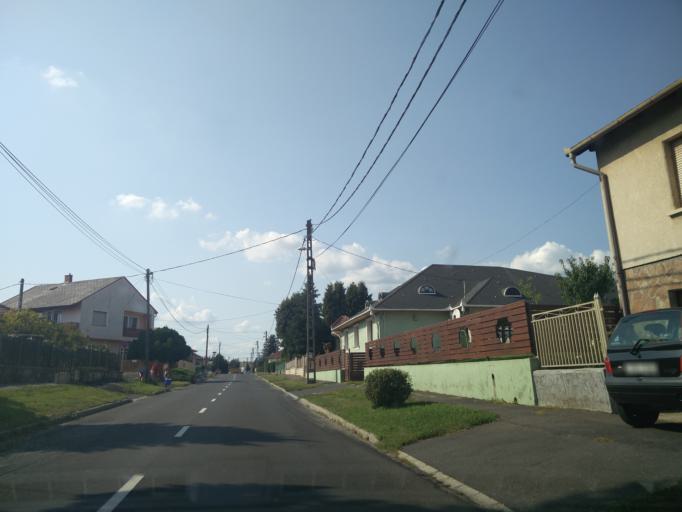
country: HU
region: Zala
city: Zalaegerszeg
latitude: 46.8691
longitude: 16.8267
